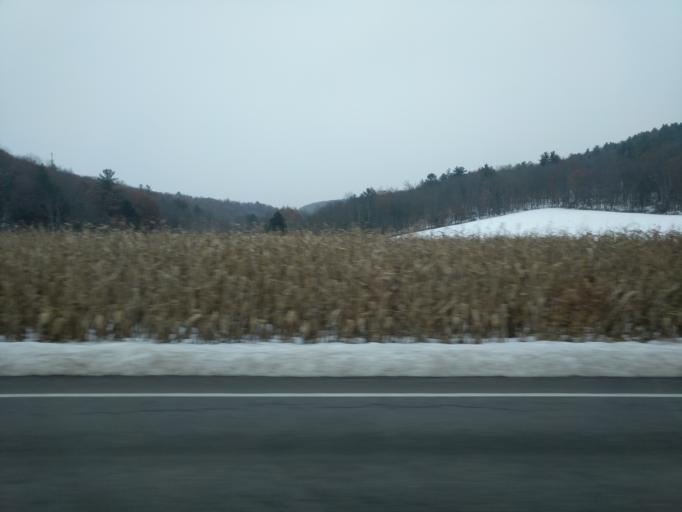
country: US
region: Pennsylvania
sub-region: Tioga County
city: Wellsboro
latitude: 41.7961
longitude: -77.3029
